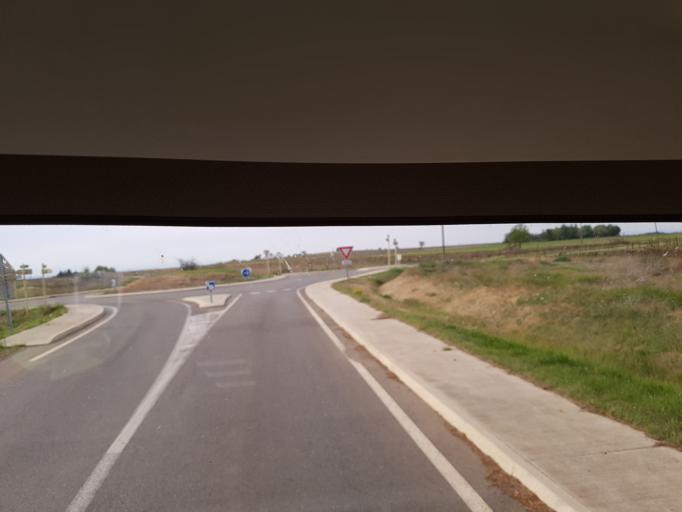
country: FR
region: Languedoc-Roussillon
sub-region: Departement de l'Herault
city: Pomerols
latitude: 43.3709
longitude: 3.4977
